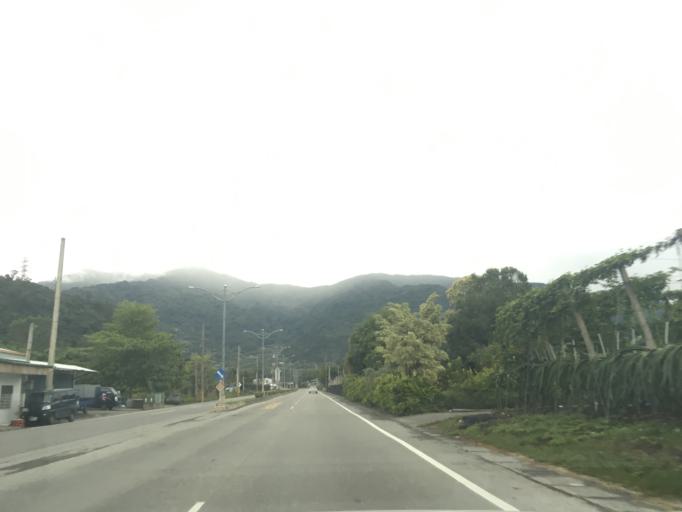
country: TW
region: Taiwan
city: Taitung City
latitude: 22.6958
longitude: 121.0446
